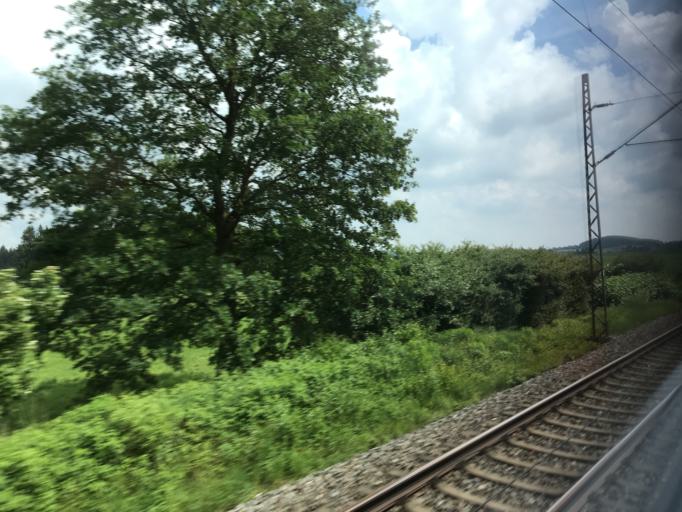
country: DE
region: Bavaria
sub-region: Swabia
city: Ustersbach
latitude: 48.3312
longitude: 10.6559
